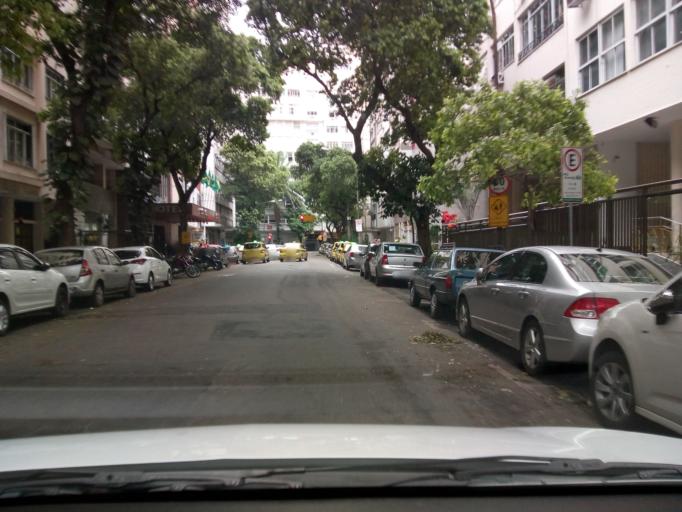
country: BR
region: Rio de Janeiro
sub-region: Rio De Janeiro
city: Rio de Janeiro
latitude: -22.9648
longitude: -43.1785
